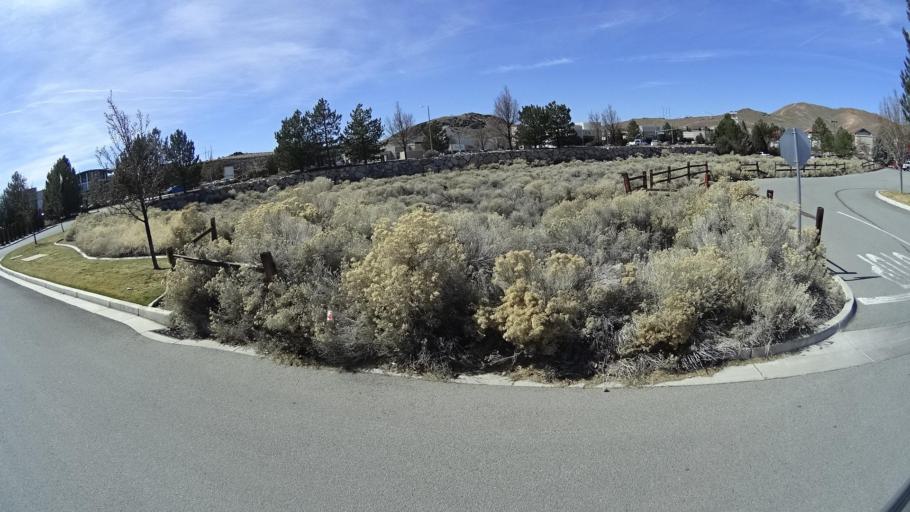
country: US
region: Nevada
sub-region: Washoe County
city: Sun Valley
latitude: 39.5765
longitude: -119.7386
